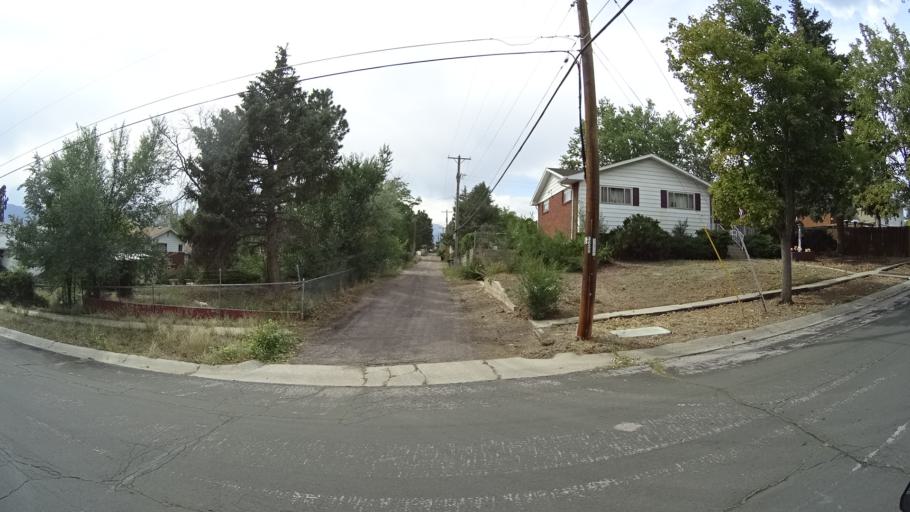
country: US
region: Colorado
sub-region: El Paso County
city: Colorado Springs
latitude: 38.8651
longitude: -104.7769
